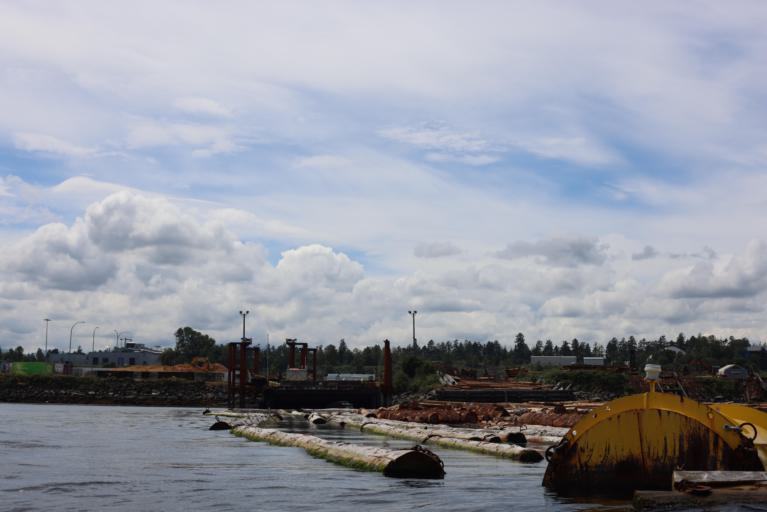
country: CA
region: British Columbia
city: Nanaimo
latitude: 49.1471
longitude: -123.8720
